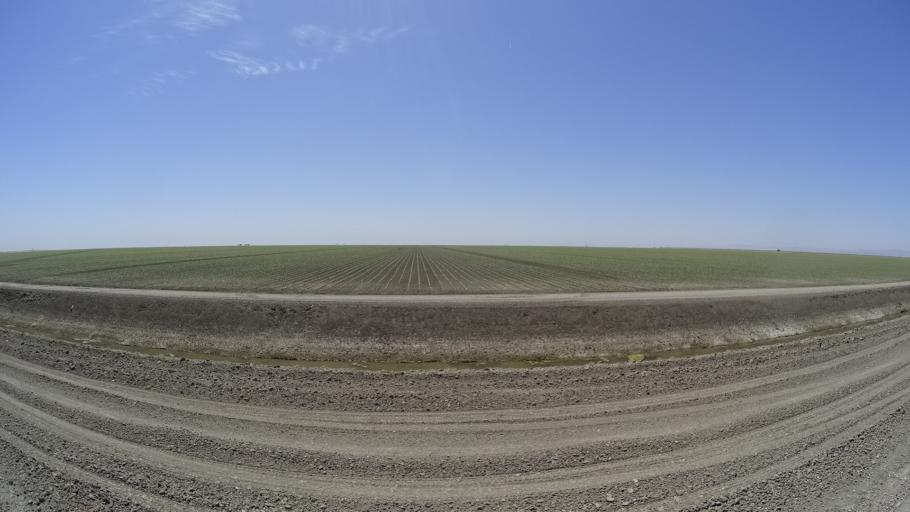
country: US
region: California
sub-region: Kings County
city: Stratford
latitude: 36.1233
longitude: -119.7047
